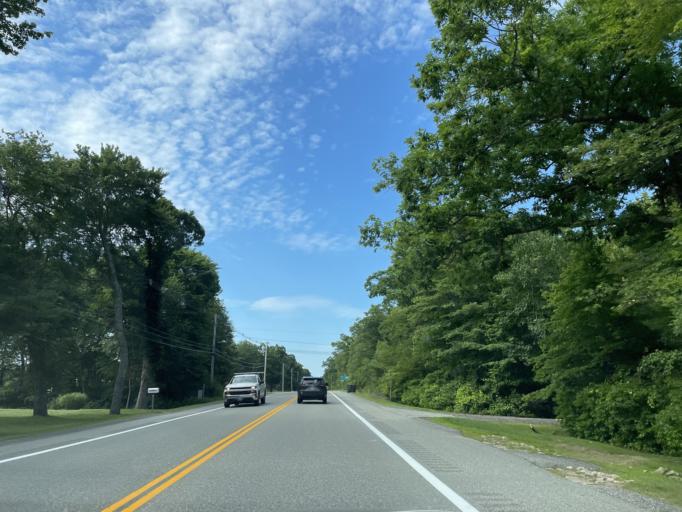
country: US
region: Rhode Island
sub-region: Kent County
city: West Greenwich
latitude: 41.6578
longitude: -71.6949
